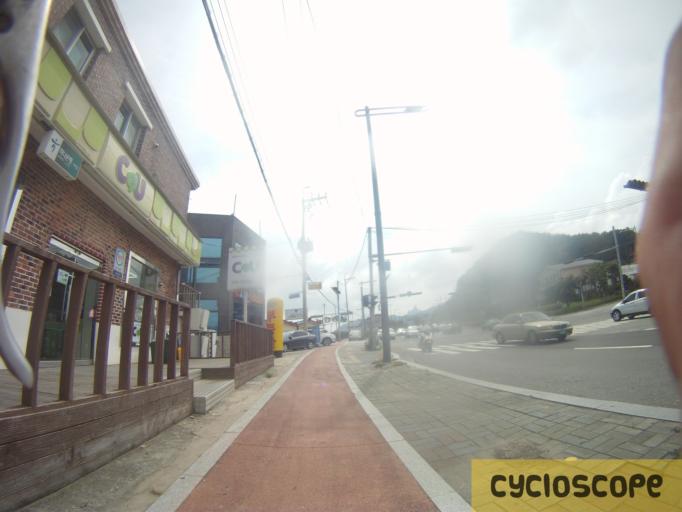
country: KR
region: Busan
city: Kijang
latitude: 35.1819
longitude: 129.2071
